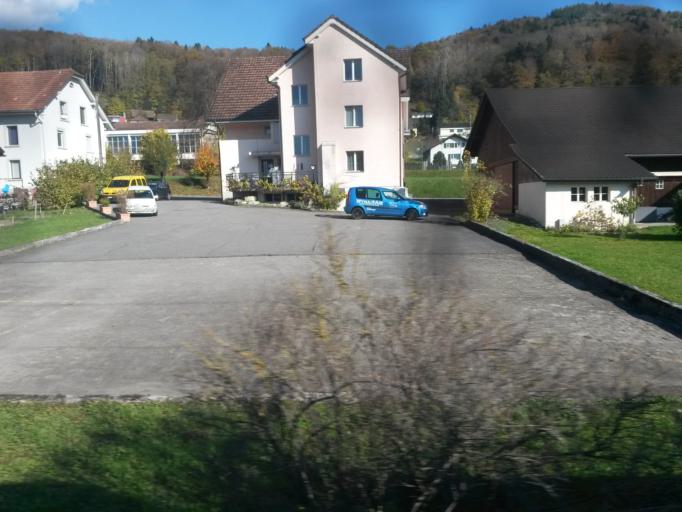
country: CH
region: Aargau
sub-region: Bezirk Kulm
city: Reinach
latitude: 47.2713
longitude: 8.1693
